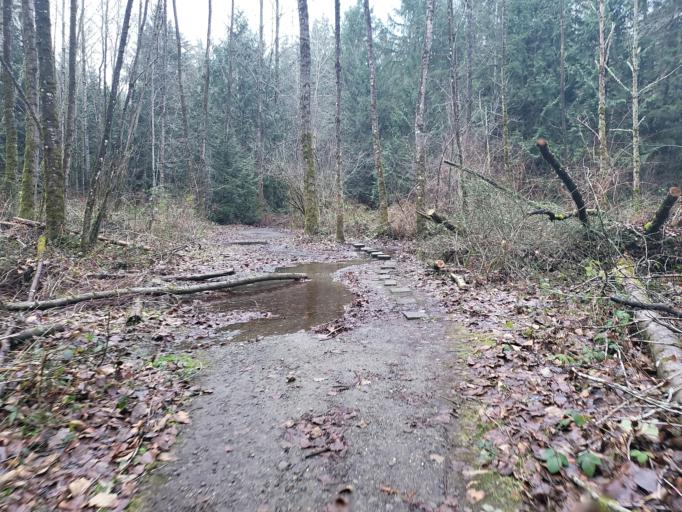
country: US
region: Washington
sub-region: King County
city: East Renton Highlands
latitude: 47.4803
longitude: -122.1421
